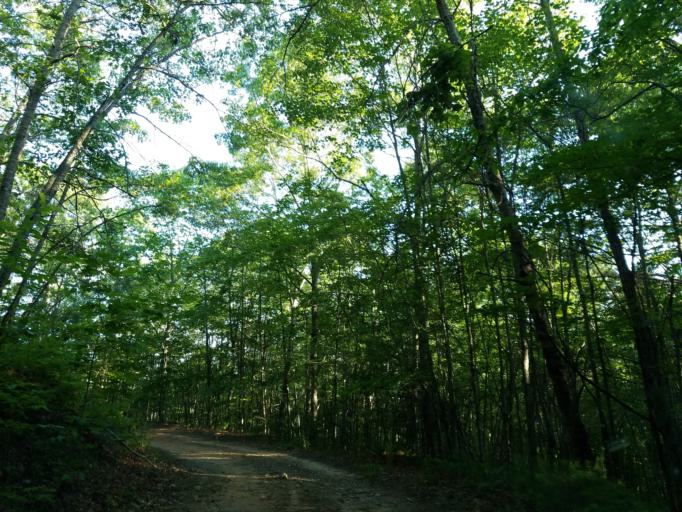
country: US
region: Georgia
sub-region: Fannin County
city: Blue Ridge
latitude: 34.8117
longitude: -84.1600
